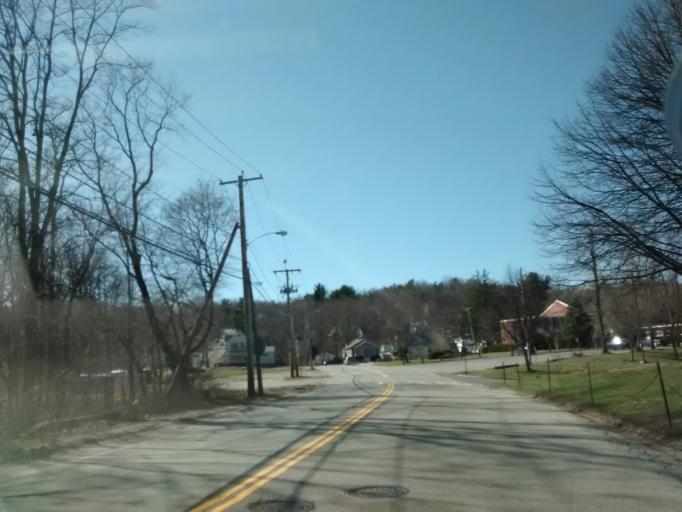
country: US
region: Massachusetts
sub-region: Worcester County
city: Worcester
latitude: 42.3047
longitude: -71.8163
